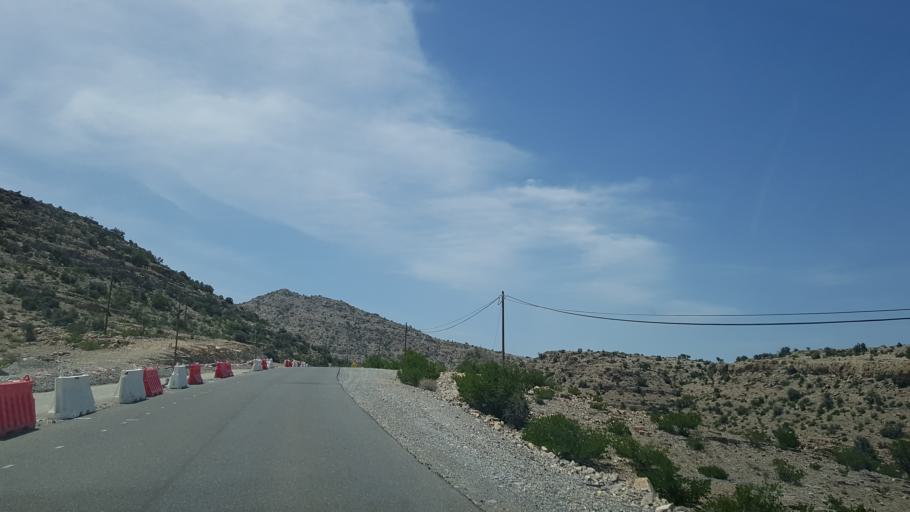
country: OM
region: Muhafazat ad Dakhiliyah
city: Izki
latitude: 23.1050
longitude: 57.6644
